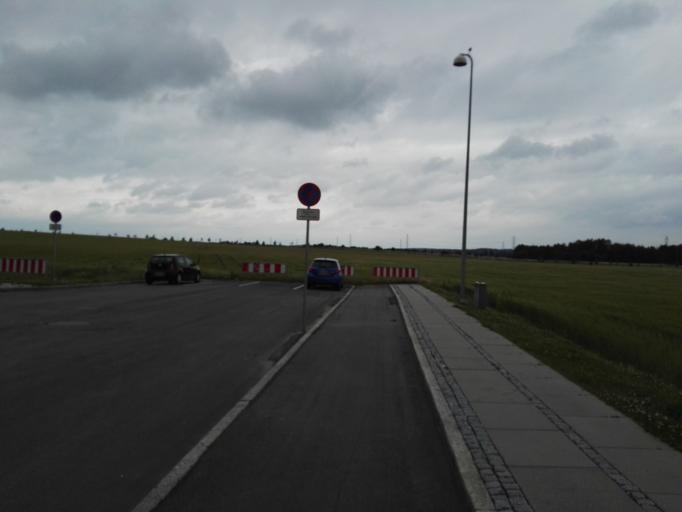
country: DK
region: Capital Region
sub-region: Egedal Kommune
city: Stenlose
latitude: 55.7803
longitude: 12.1884
